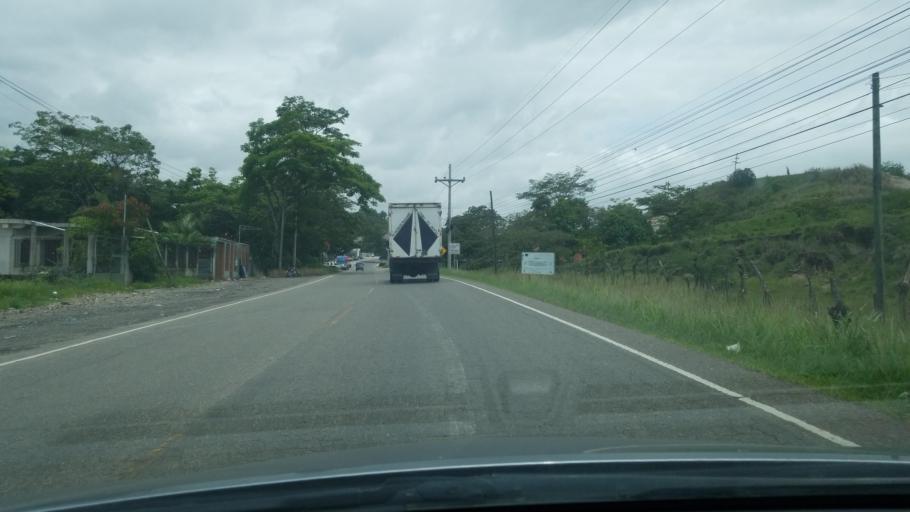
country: HN
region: Copan
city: Cucuyagua
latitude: 14.6621
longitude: -88.8716
